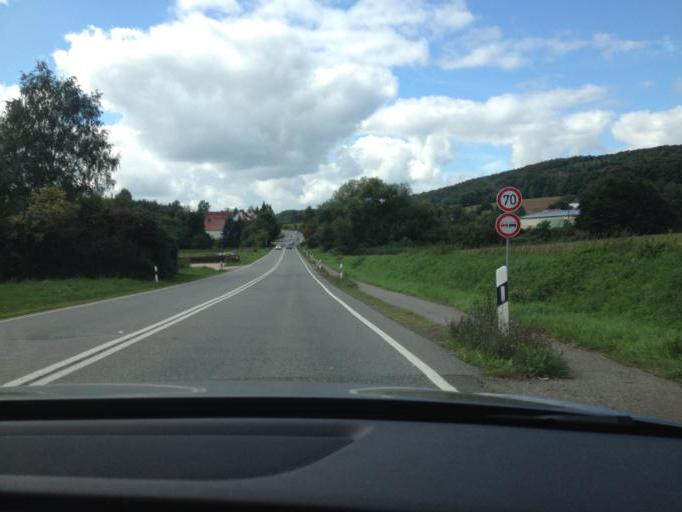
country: DE
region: Saarland
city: Namborn
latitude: 49.5269
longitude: 7.1681
